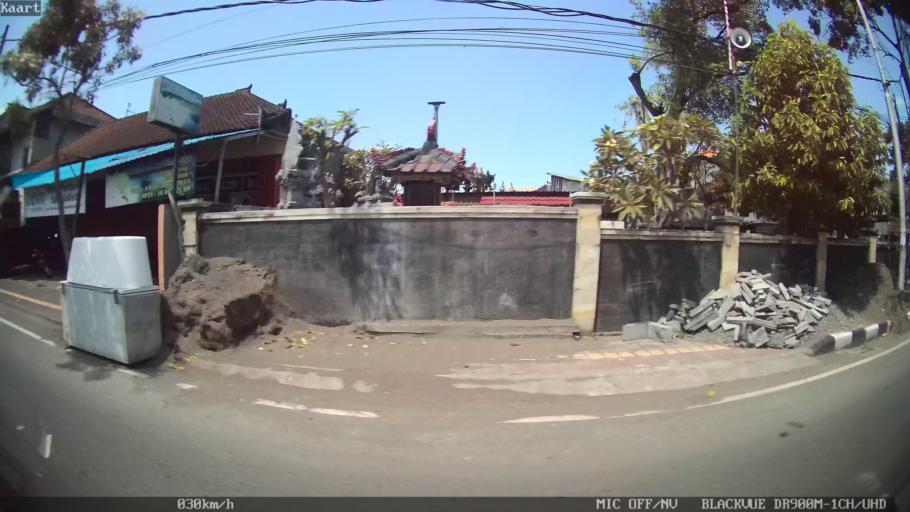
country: ID
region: Bali
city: Denpasar
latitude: -8.6654
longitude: 115.1896
